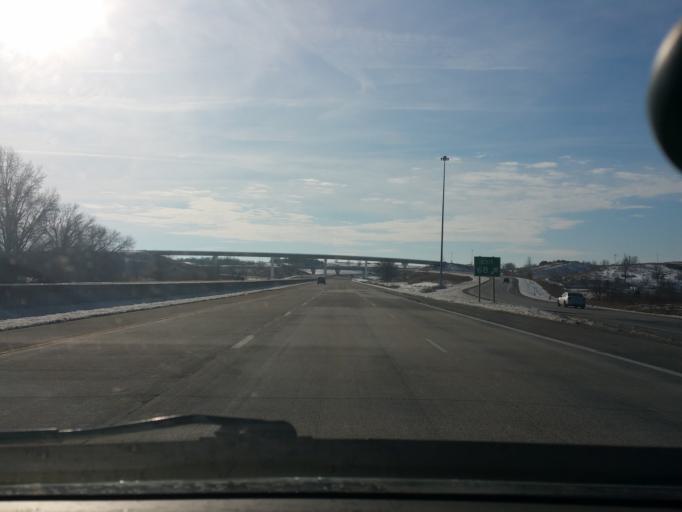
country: US
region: Iowa
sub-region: Polk County
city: West Des Moines
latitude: 41.5300
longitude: -93.7738
